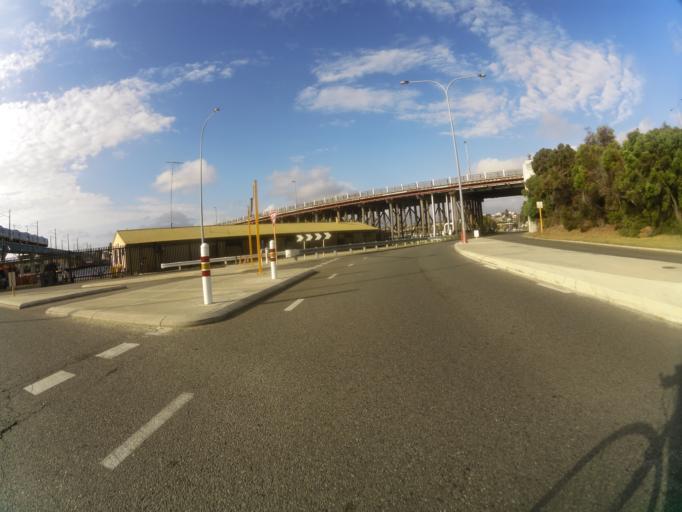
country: AU
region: Western Australia
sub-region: Fremantle
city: North Fremantle
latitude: -32.0425
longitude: 115.7541
